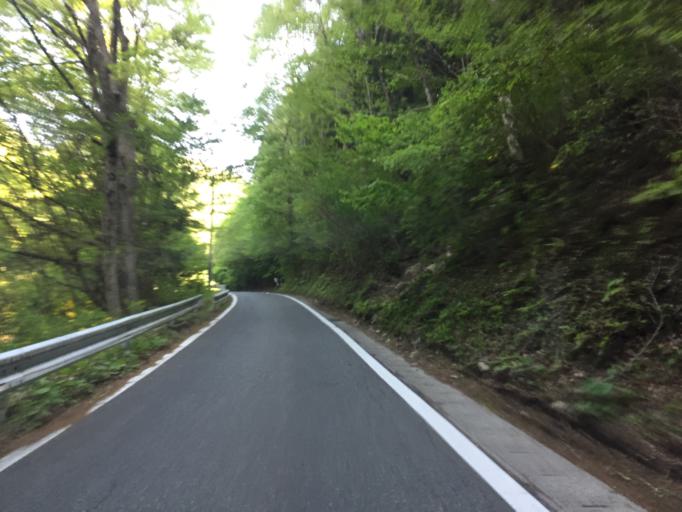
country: JP
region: Fukushima
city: Namie
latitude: 37.5228
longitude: 140.8520
